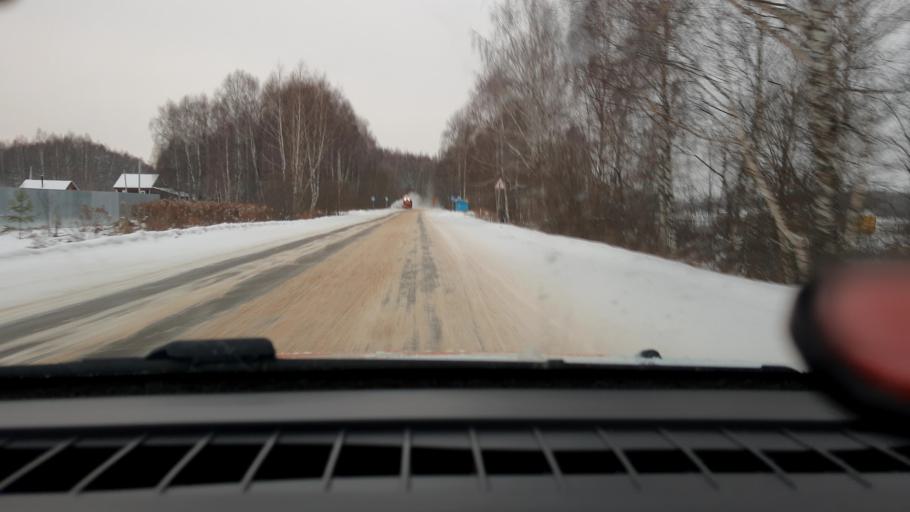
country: RU
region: Nizjnij Novgorod
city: Pamyat' Parizhskoy Kommuny
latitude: 56.2501
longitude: 44.4811
